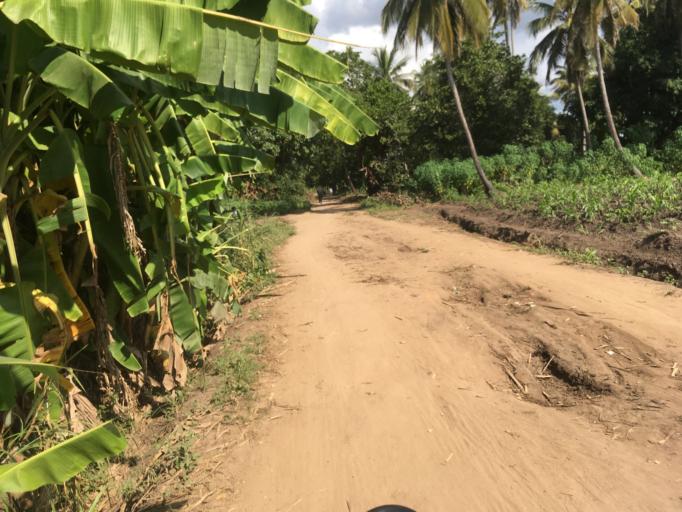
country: MZ
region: Zambezia
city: Quelimane
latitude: -17.6475
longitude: 36.6853
